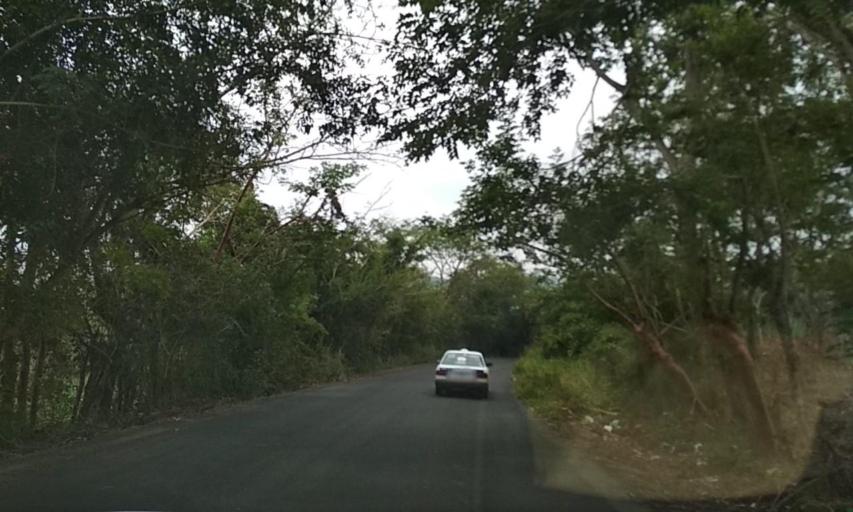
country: MX
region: Veracruz
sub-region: Coatzintla
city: Manuel Maria Contreras
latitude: 20.4465
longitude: -97.4996
